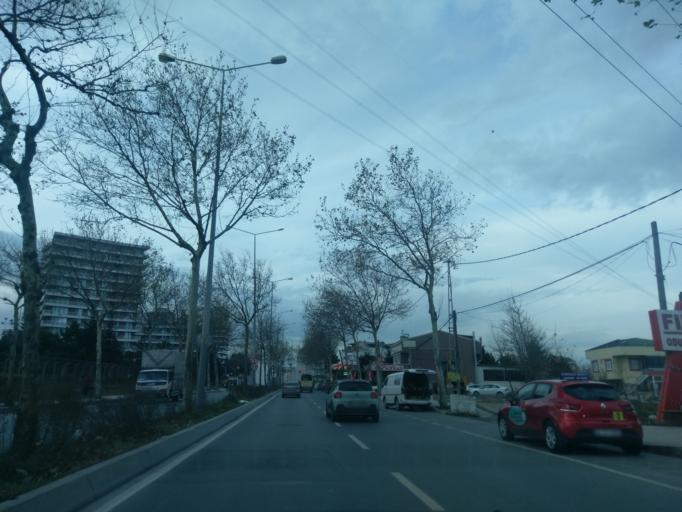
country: TR
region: Istanbul
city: Esenyurt
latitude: 41.0679
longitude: 28.6681
